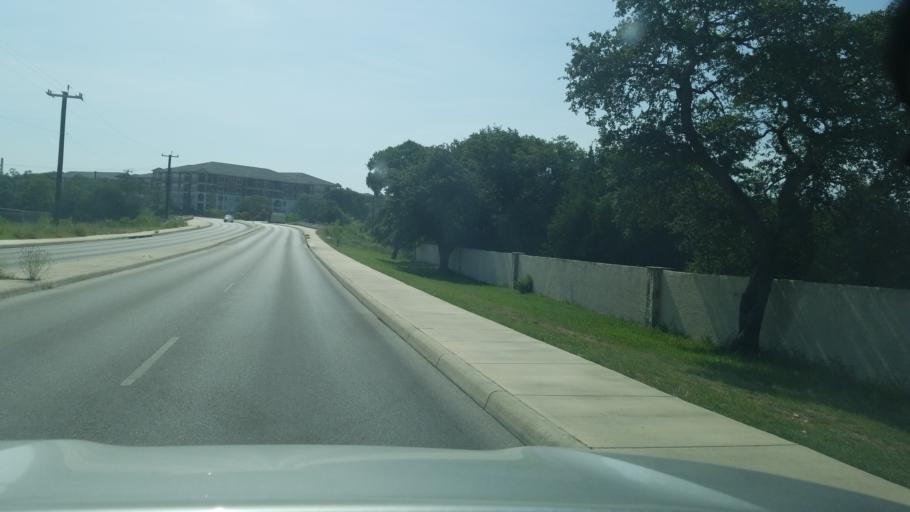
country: US
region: Texas
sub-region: Bexar County
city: Timberwood Park
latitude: 29.6680
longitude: -98.4672
